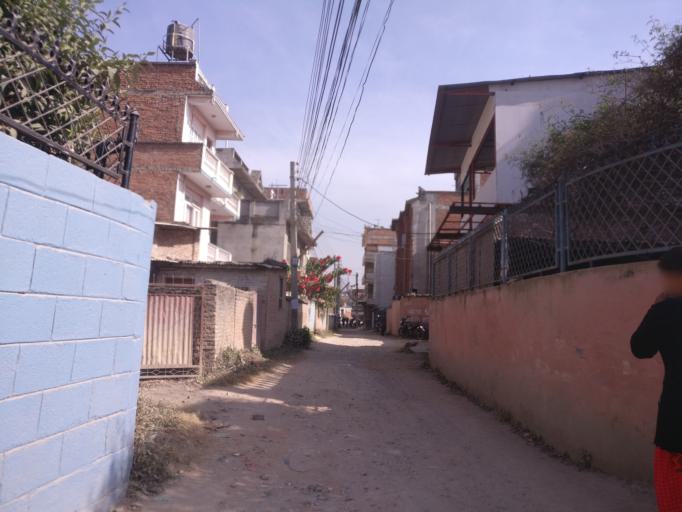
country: NP
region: Central Region
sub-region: Bagmati Zone
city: Patan
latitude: 27.6713
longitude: 85.3367
